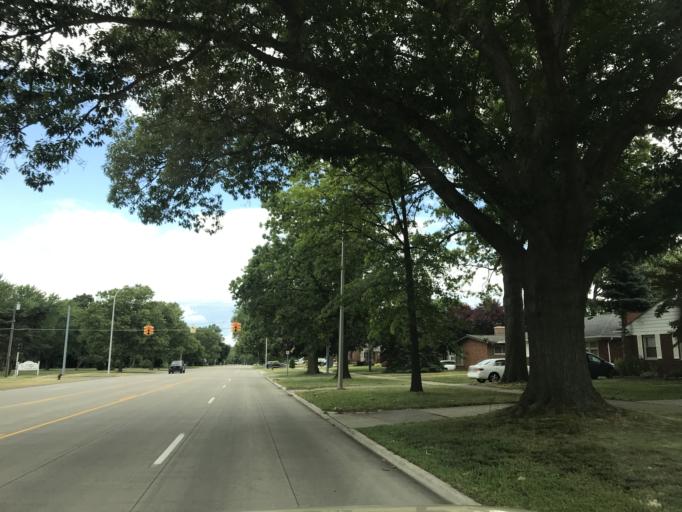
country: US
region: Michigan
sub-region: Wayne County
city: Dearborn Heights
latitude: 42.3287
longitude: -83.2614
